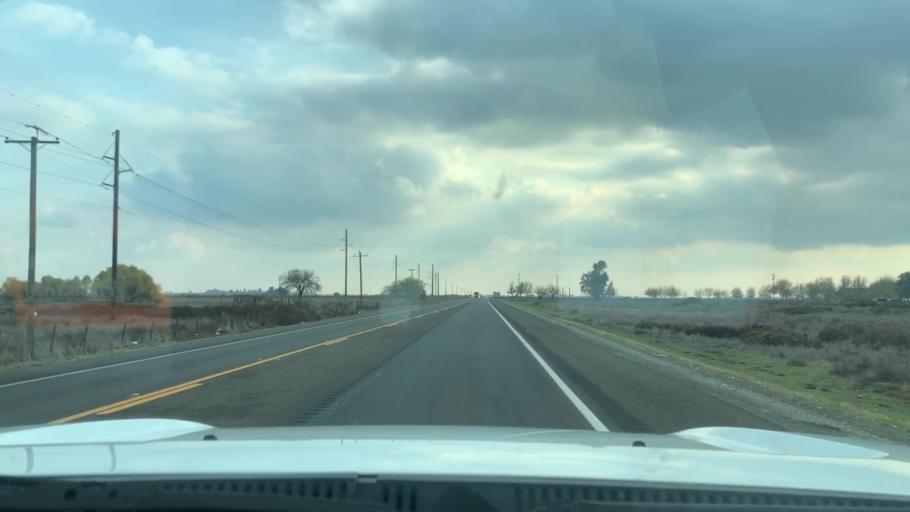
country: US
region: California
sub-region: Kings County
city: Stratford
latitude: 36.2389
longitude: -119.8165
